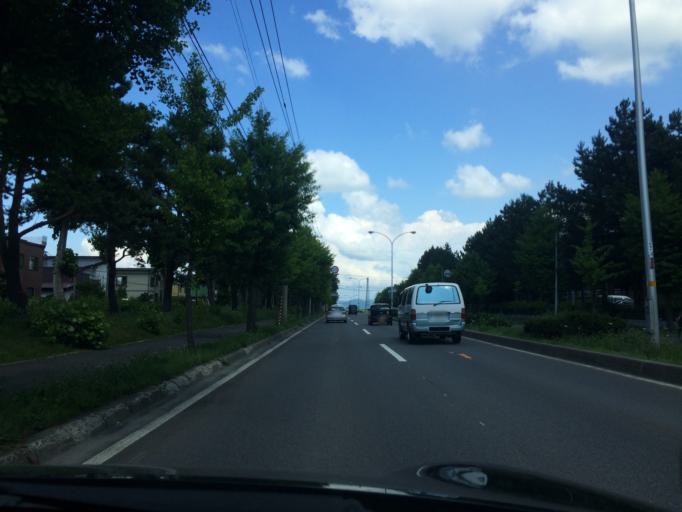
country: JP
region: Hokkaido
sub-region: Asahikawa-shi
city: Asahikawa
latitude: 43.7313
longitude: 142.3837
